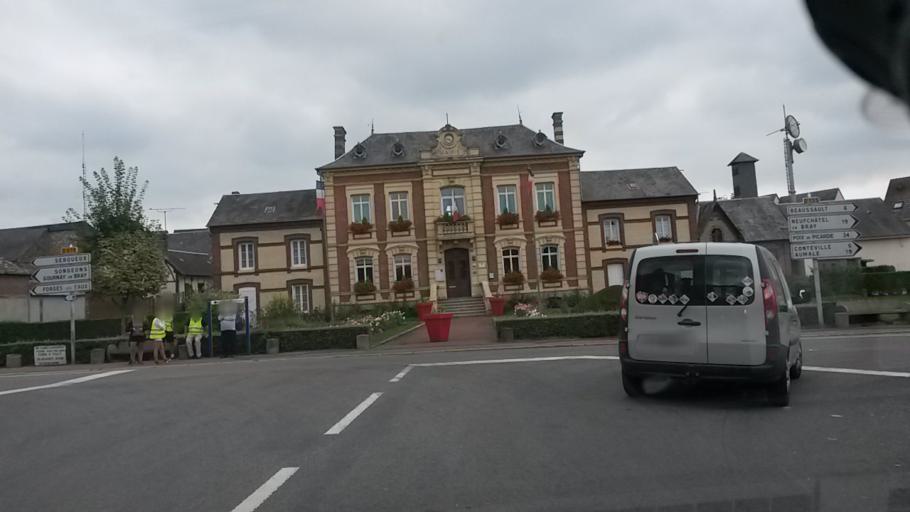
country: FR
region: Haute-Normandie
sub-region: Departement de la Seine-Maritime
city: Gaillefontaine
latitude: 49.6530
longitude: 1.6157
